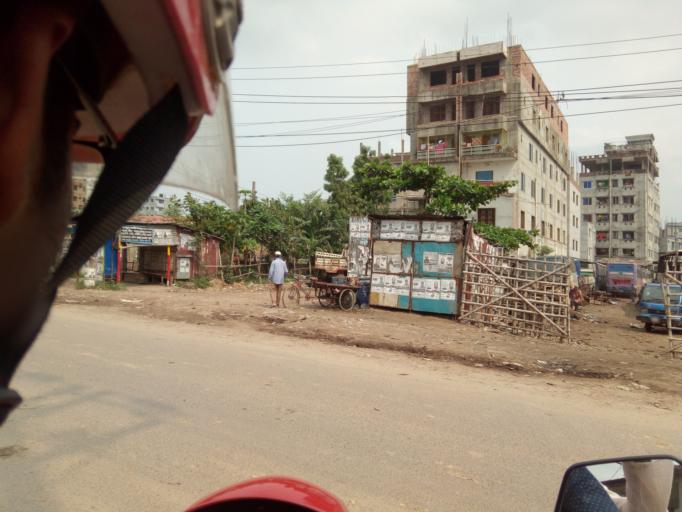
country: BD
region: Dhaka
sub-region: Dhaka
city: Dhaka
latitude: 23.7121
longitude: 90.4490
